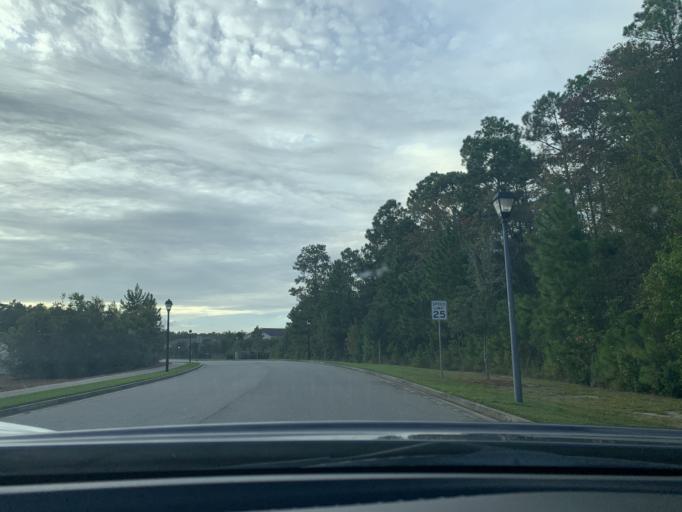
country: US
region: Georgia
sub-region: Chatham County
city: Pooler
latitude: 32.0748
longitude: -81.2603
